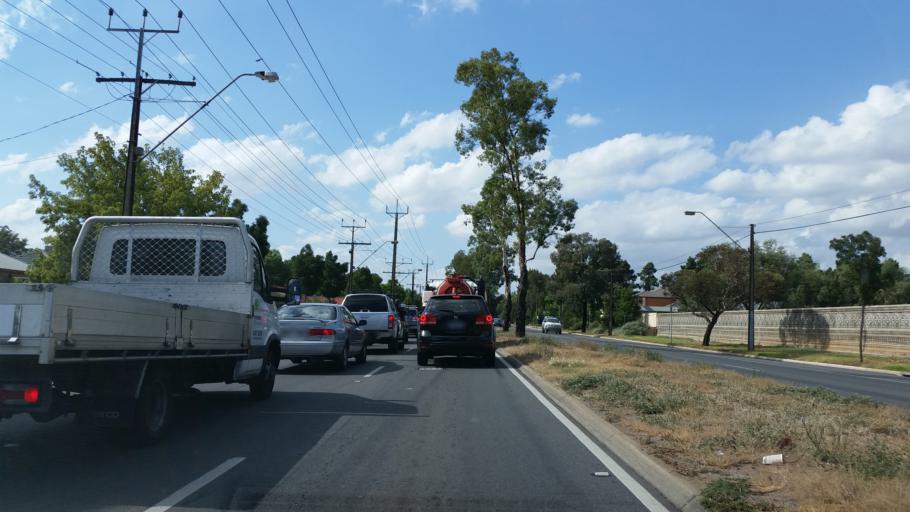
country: AU
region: South Australia
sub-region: Salisbury
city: Salisbury
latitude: -34.7828
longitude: 138.6231
